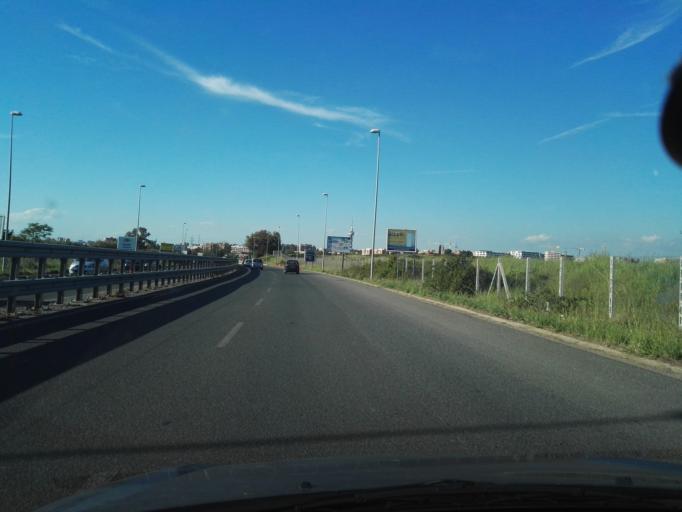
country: IT
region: Latium
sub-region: Citta metropolitana di Roma Capitale
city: Selcetta
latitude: 41.7829
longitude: 12.4813
